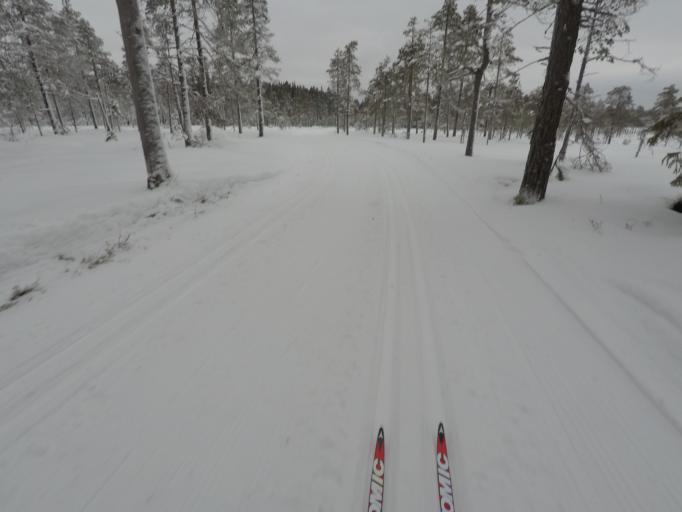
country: SE
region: Vaermland
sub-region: Filipstads Kommun
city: Lesjofors
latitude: 60.1590
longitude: 14.4456
